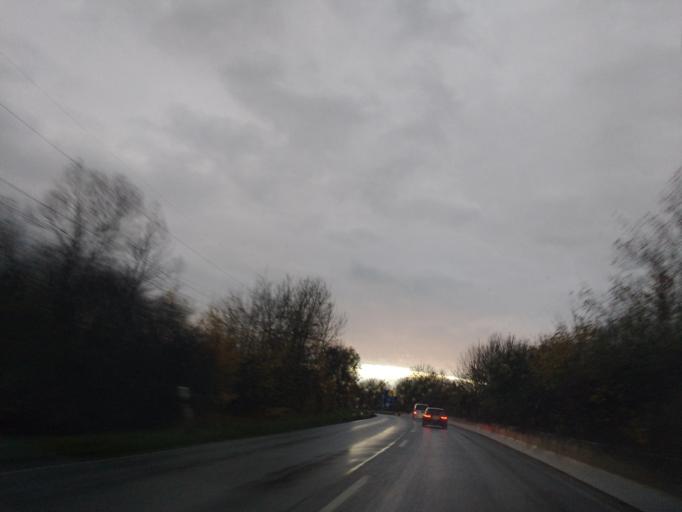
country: DE
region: Hesse
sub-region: Regierungsbezirk Kassel
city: Baunatal
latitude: 51.2461
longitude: 9.4296
